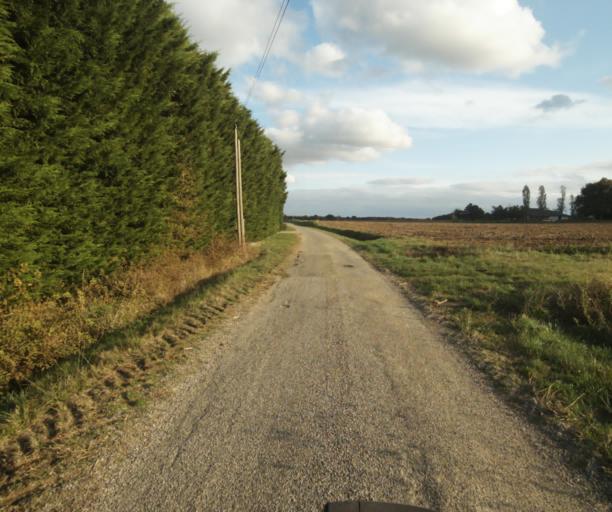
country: FR
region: Midi-Pyrenees
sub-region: Departement de la Haute-Garonne
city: Launac
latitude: 43.8148
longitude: 1.1381
